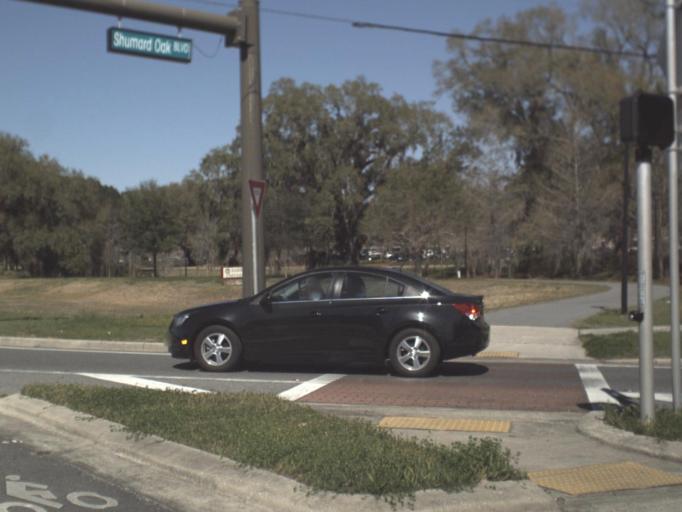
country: US
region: Florida
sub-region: Leon County
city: Tallahassee
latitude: 30.3872
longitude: -84.2354
